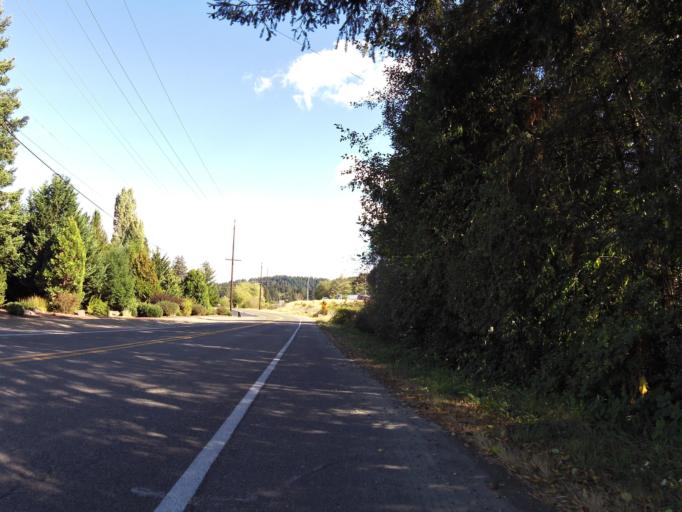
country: US
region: Washington
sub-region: Thurston County
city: Olympia
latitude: 47.0485
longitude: -122.9957
